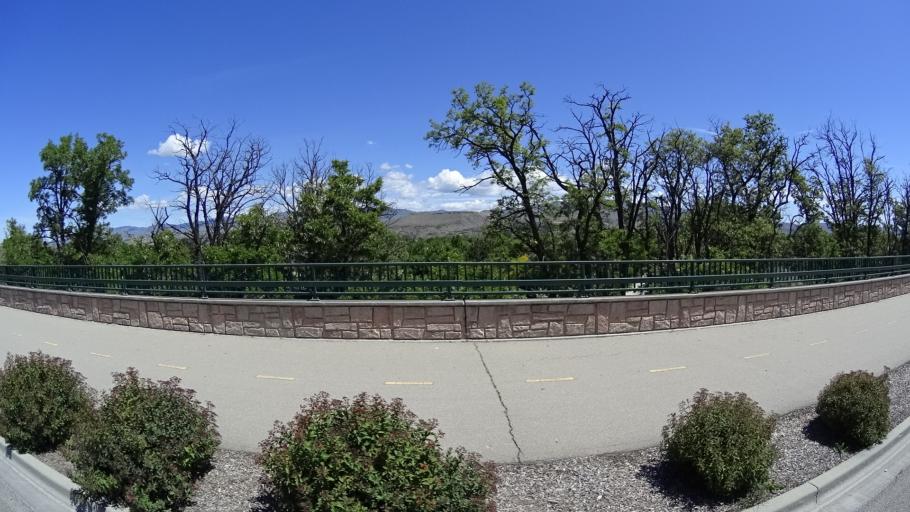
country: US
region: Idaho
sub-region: Ada County
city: Boise
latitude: 43.5700
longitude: -116.1855
